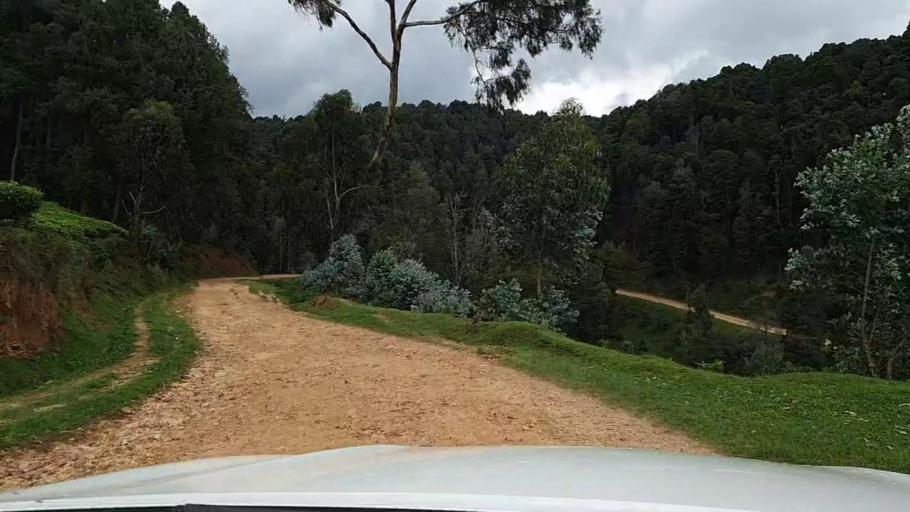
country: RW
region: Western Province
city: Kibuye
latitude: -2.2893
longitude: 29.3699
